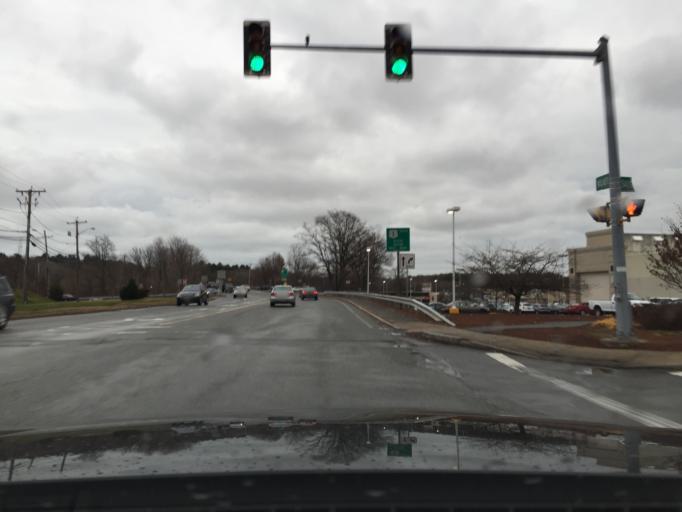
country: US
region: Massachusetts
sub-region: Essex County
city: Saugus
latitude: 42.4905
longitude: -71.0187
